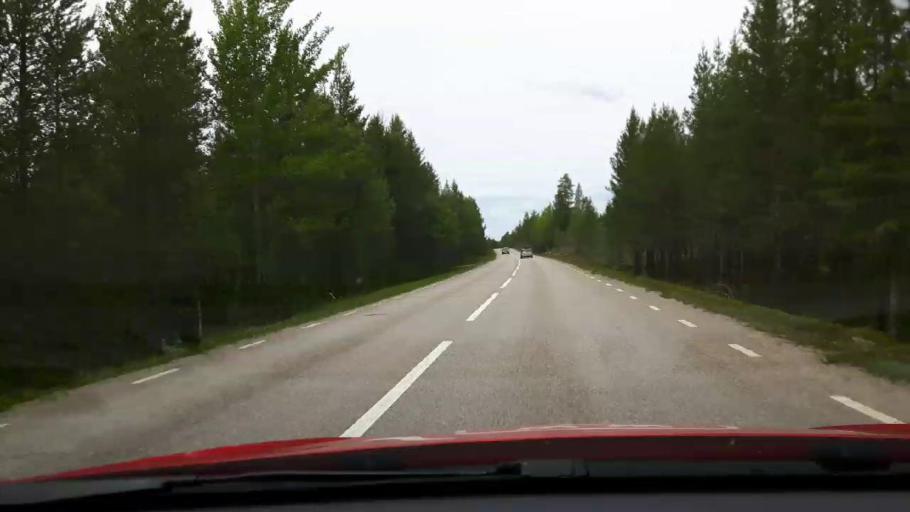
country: SE
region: Jaemtland
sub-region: Harjedalens Kommun
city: Sveg
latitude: 62.2365
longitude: 13.8524
